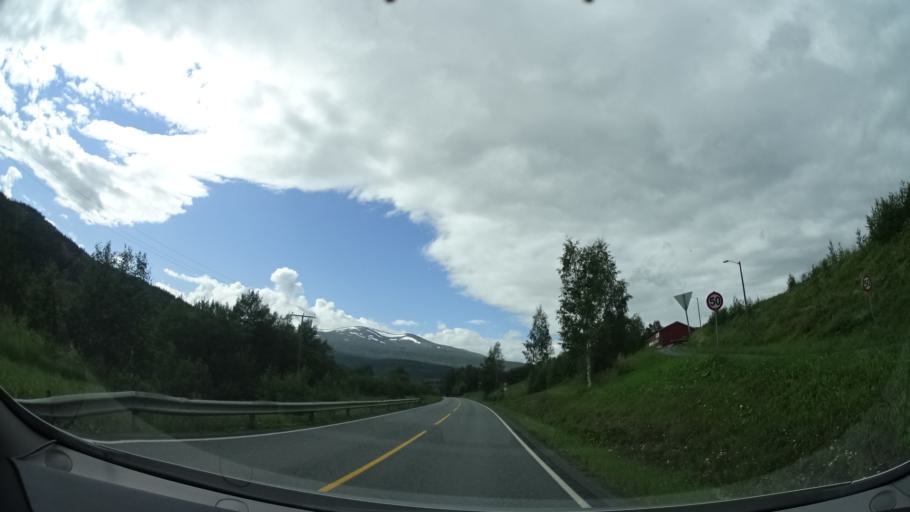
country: NO
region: Nord-Trondelag
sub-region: Meraker
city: Meraker
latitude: 63.4059
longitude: 11.7636
